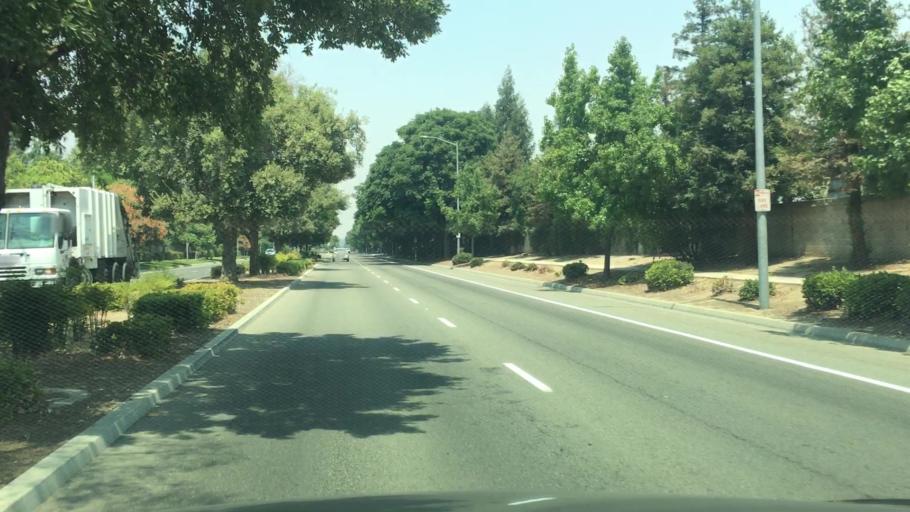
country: US
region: California
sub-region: Fresno County
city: Clovis
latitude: 36.8478
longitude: -119.7111
